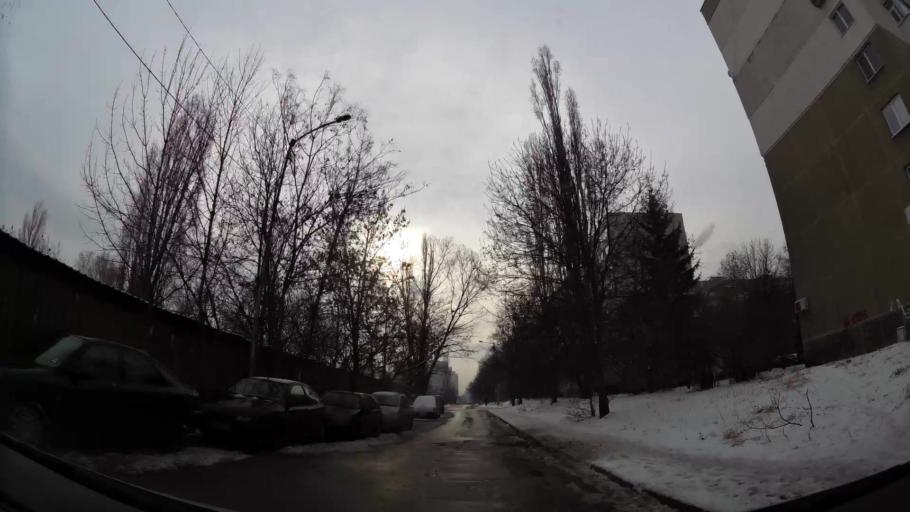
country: BG
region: Sofia-Capital
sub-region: Stolichna Obshtina
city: Sofia
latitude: 42.7164
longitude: 23.3054
